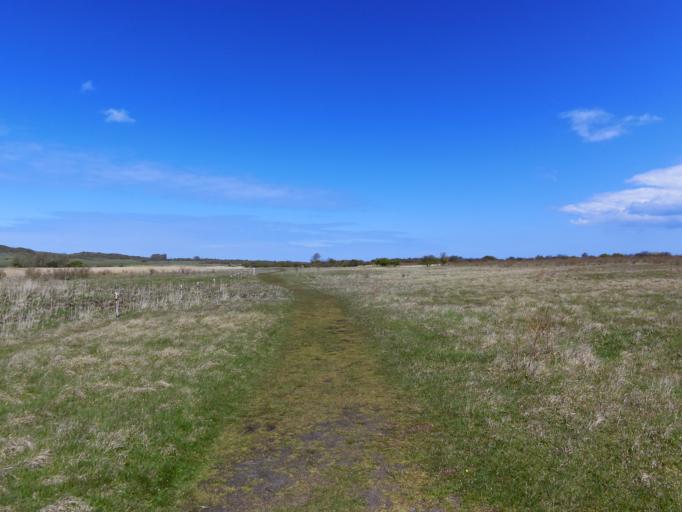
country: DE
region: Mecklenburg-Vorpommern
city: Hiddensee
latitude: 54.5924
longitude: 13.1414
